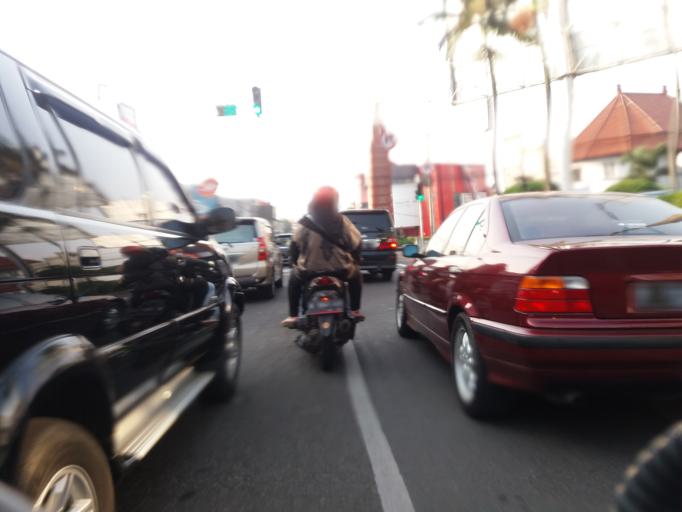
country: ID
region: West Java
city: Bandung
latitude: -6.9229
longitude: 107.6175
